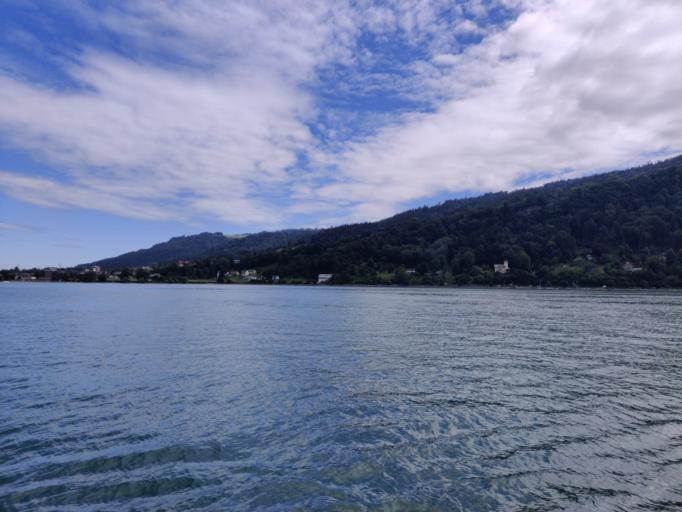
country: AT
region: Vorarlberg
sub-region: Politischer Bezirk Bregenz
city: Bregenz
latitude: 47.5147
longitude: 9.7435
